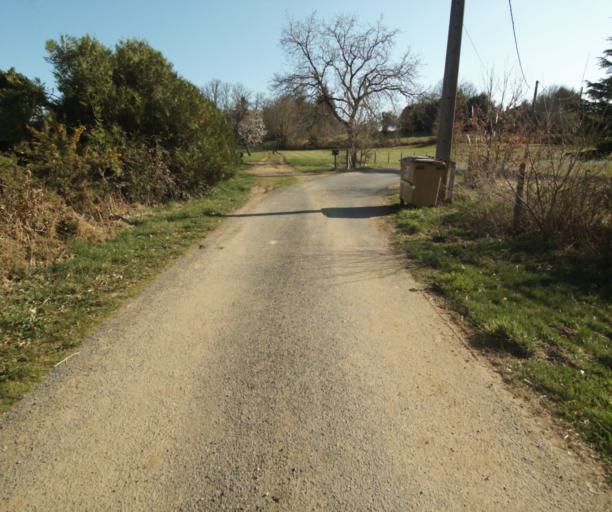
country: FR
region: Limousin
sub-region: Departement de la Correze
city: Saint-Clement
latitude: 45.3196
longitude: 1.6806
